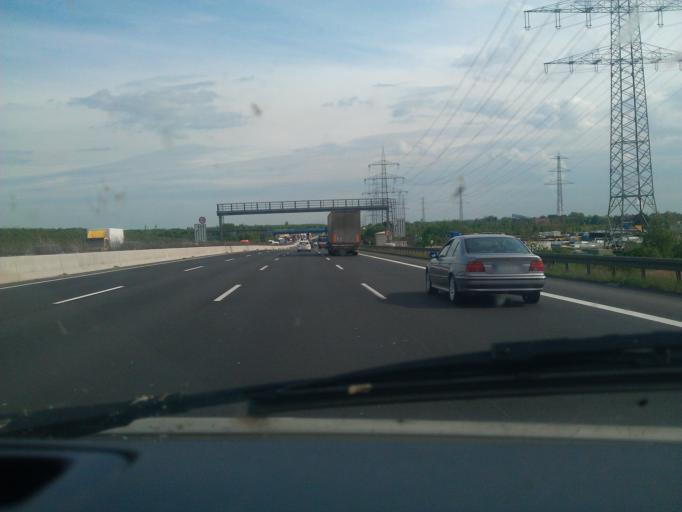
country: DE
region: North Rhine-Westphalia
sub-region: Regierungsbezirk Dusseldorf
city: Kaarst
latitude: 51.2154
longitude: 6.6440
